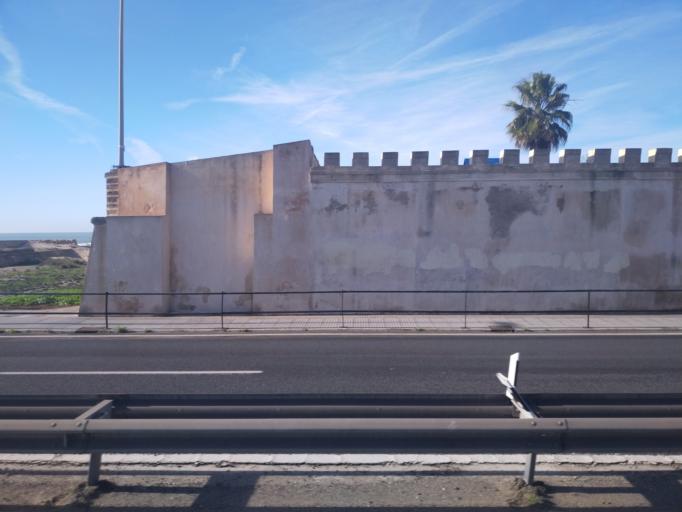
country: ES
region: Andalusia
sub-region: Provincia de Cadiz
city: Cadiz
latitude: 36.4945
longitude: -6.2701
